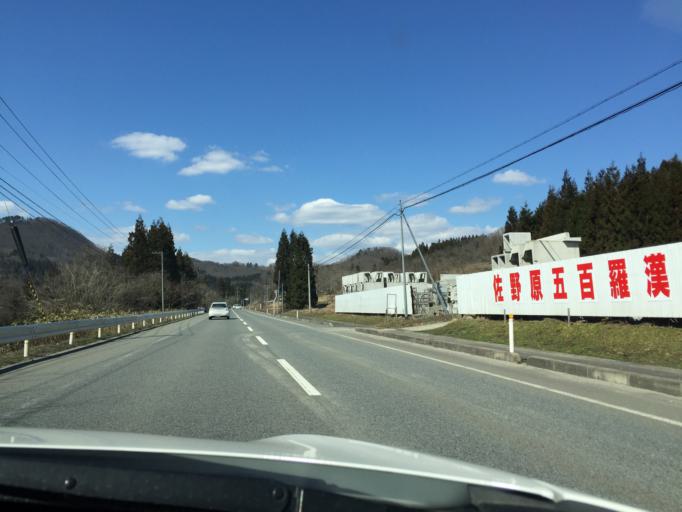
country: JP
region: Yamagata
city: Nagai
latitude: 38.2341
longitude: 140.0906
